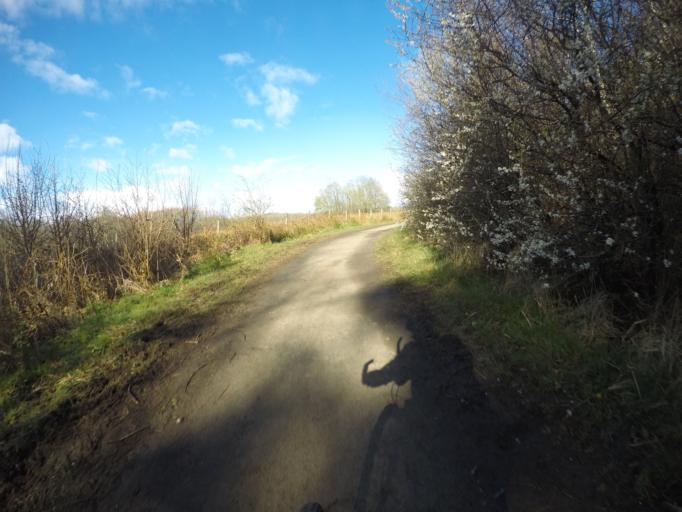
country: GB
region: Scotland
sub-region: North Ayrshire
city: Irvine
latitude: 55.6401
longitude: -4.6571
